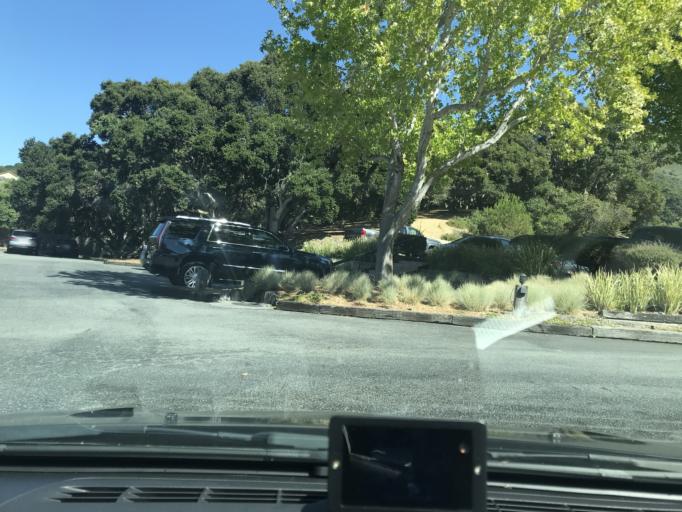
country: US
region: California
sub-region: Monterey County
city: Carmel Valley Village
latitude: 36.5173
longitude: -121.7995
